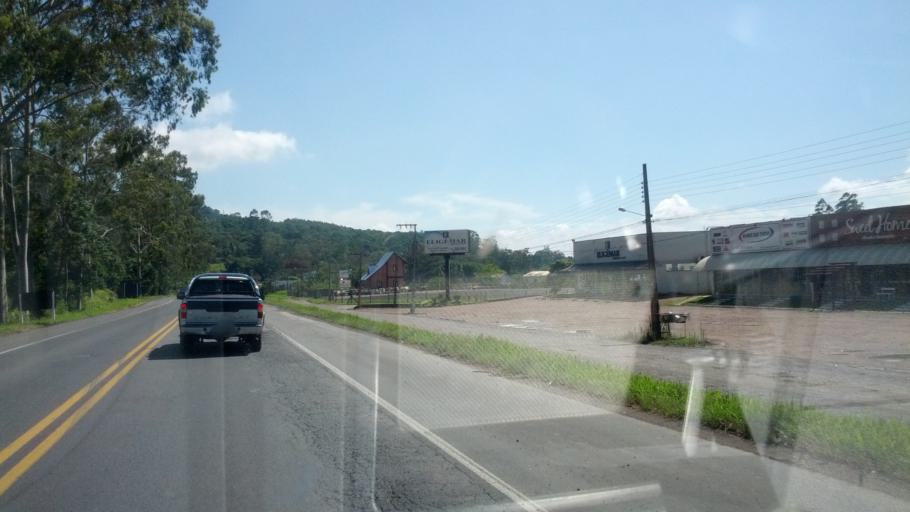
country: BR
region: Santa Catarina
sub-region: Rio Do Sul
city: Rio do Sul
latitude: -27.1925
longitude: -49.6225
